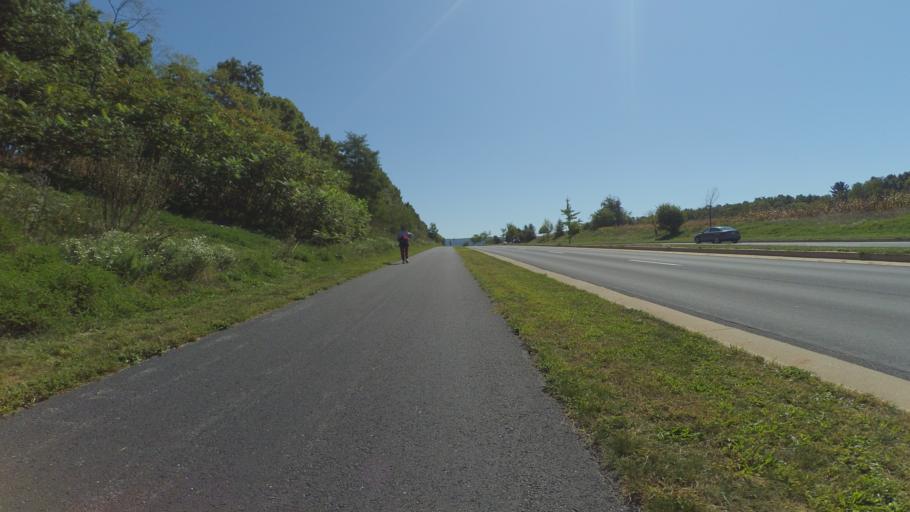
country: US
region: Pennsylvania
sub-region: Centre County
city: State College
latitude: 40.7879
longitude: -77.8905
